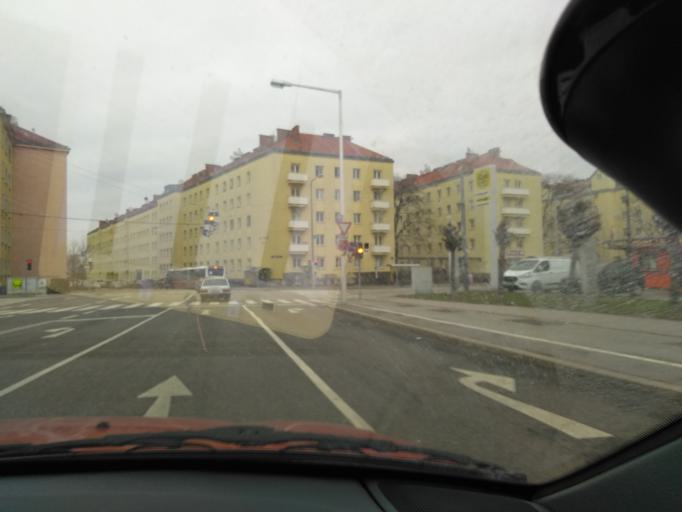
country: AT
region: Lower Austria
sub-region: Politischer Bezirk Modling
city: Vosendorf
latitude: 48.1707
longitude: 16.3372
